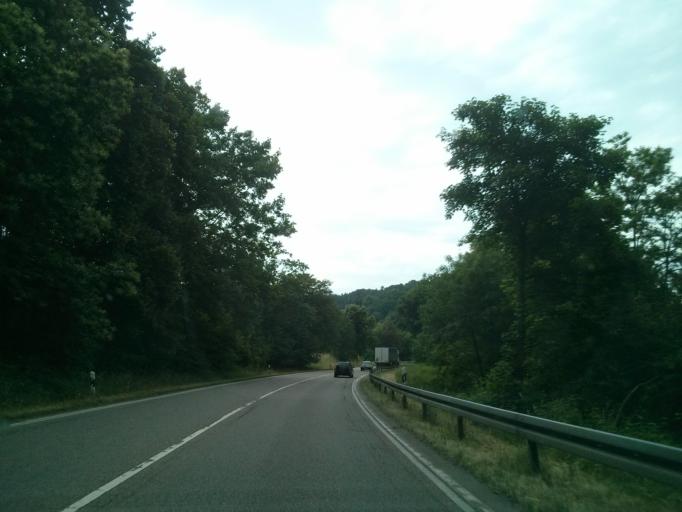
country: DE
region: Baden-Wuerttemberg
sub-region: Karlsruhe Region
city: Gaggenau
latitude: 48.7871
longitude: 8.3278
